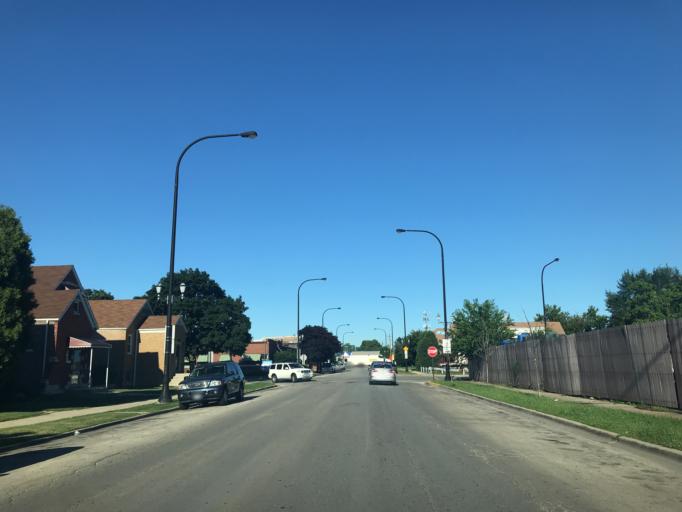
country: US
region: Illinois
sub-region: Cook County
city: Cicero
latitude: 41.8457
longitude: -87.7475
